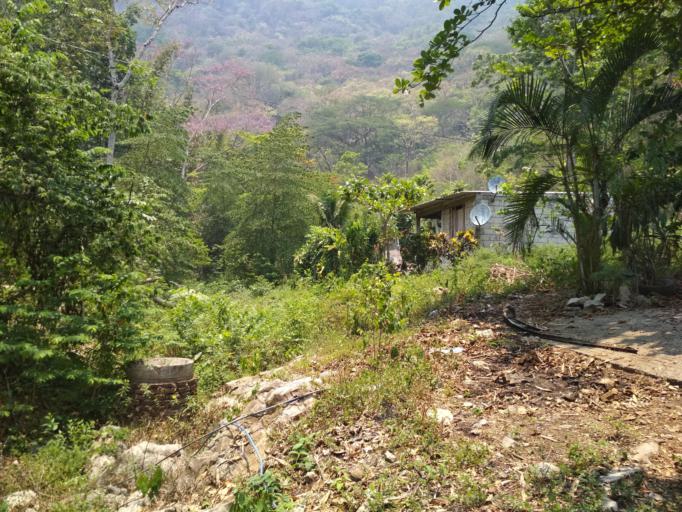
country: MX
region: Veracruz
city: Cosolapa
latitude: 18.6013
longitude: -96.6911
